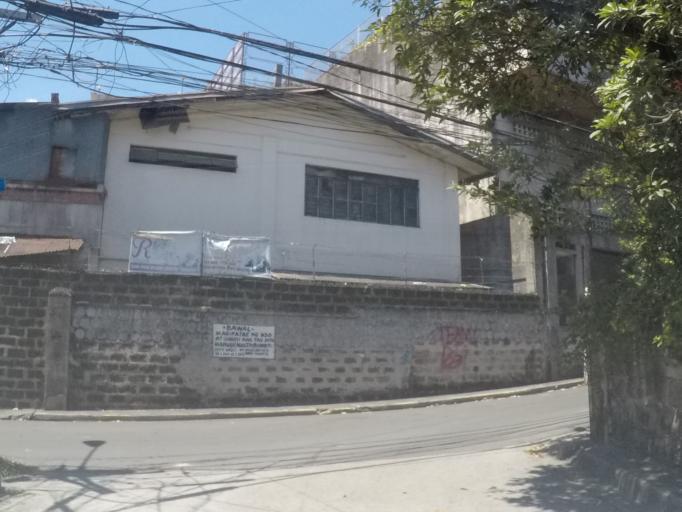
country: PH
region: Metro Manila
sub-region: San Juan
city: San Juan
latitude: 14.5988
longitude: 121.0278
